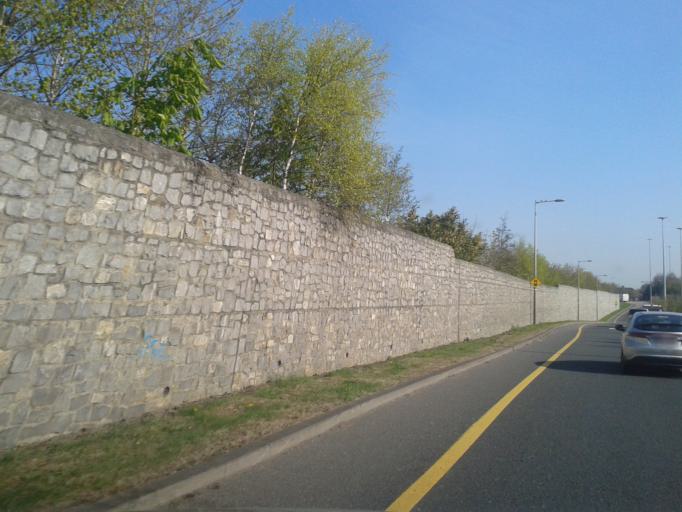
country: IE
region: Leinster
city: Beaumont
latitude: 53.3942
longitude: -6.2410
